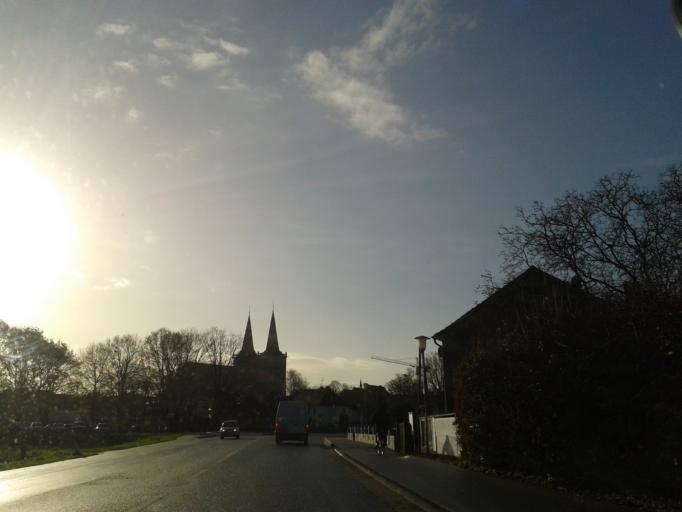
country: DE
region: North Rhine-Westphalia
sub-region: Regierungsbezirk Dusseldorf
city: Xanten
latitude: 51.6662
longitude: 6.4534
